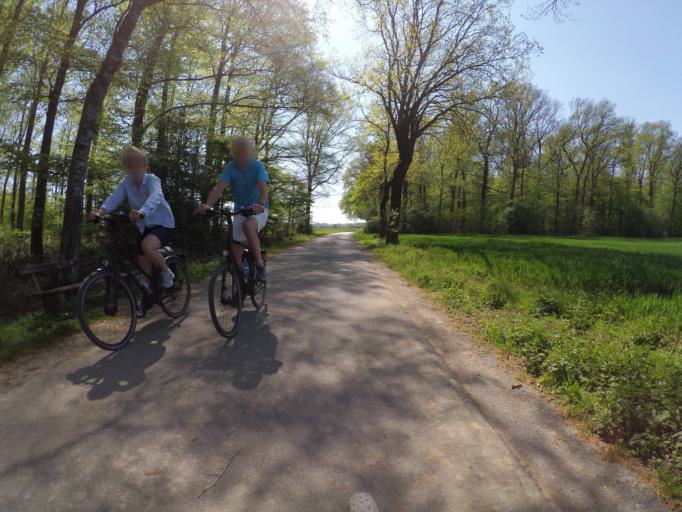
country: DE
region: North Rhine-Westphalia
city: Ludinghausen
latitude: 51.7546
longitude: 7.4415
